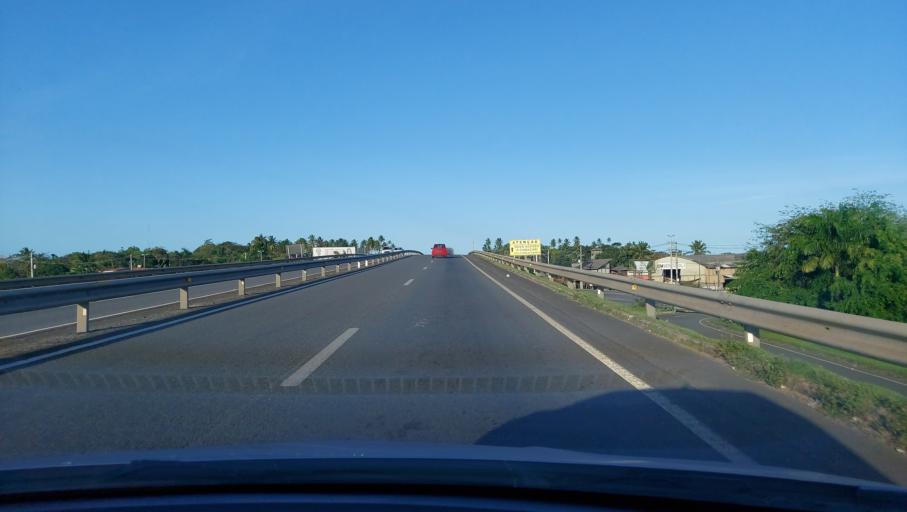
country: BR
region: Bahia
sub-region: Lauro De Freitas
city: Lauro de Freitas
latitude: -12.8187
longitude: -38.2481
